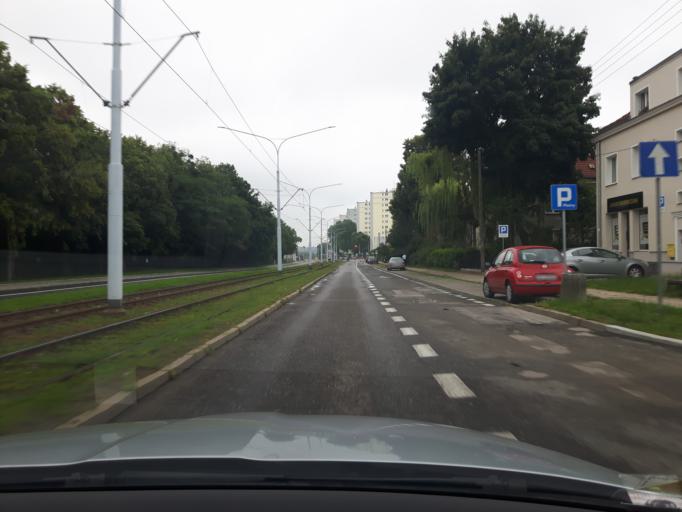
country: PL
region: Pomeranian Voivodeship
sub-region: Sopot
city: Sopot
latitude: 54.4011
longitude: 18.5667
